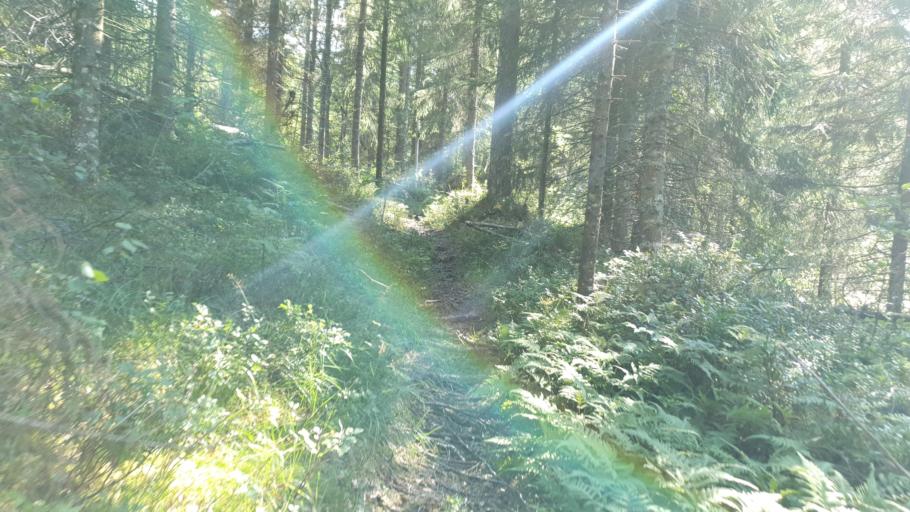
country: NO
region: Nord-Trondelag
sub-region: Levanger
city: Levanger
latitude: 63.6897
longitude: 11.2642
